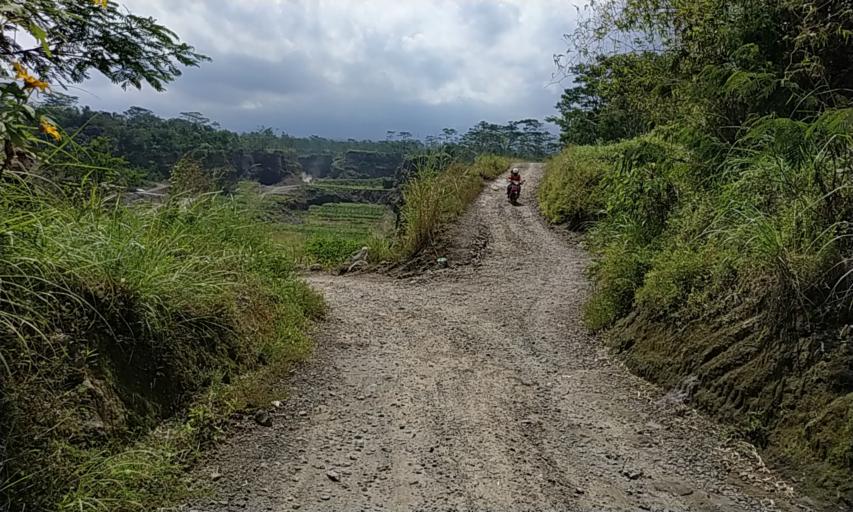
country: ID
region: Central Java
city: Jogonalan
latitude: -7.6283
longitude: 110.4849
